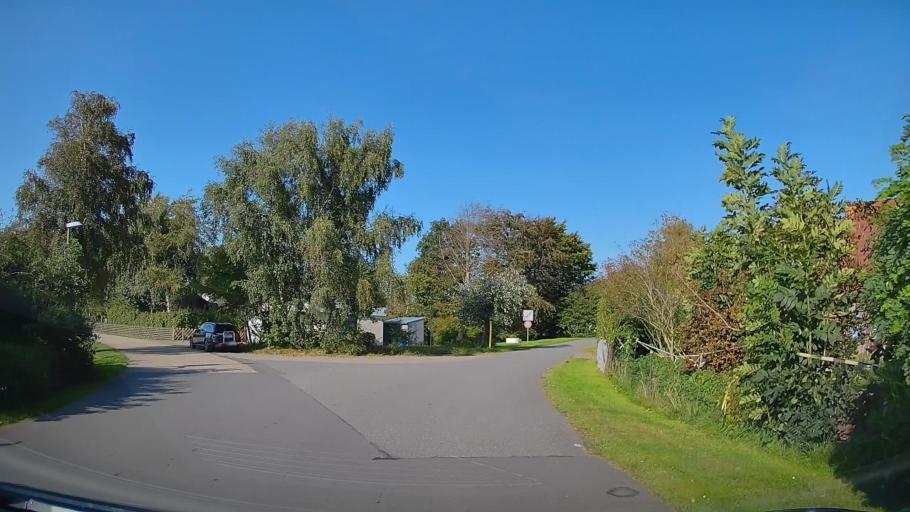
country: DE
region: Lower Saxony
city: Padingbuttel
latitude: 53.7124
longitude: 8.5128
